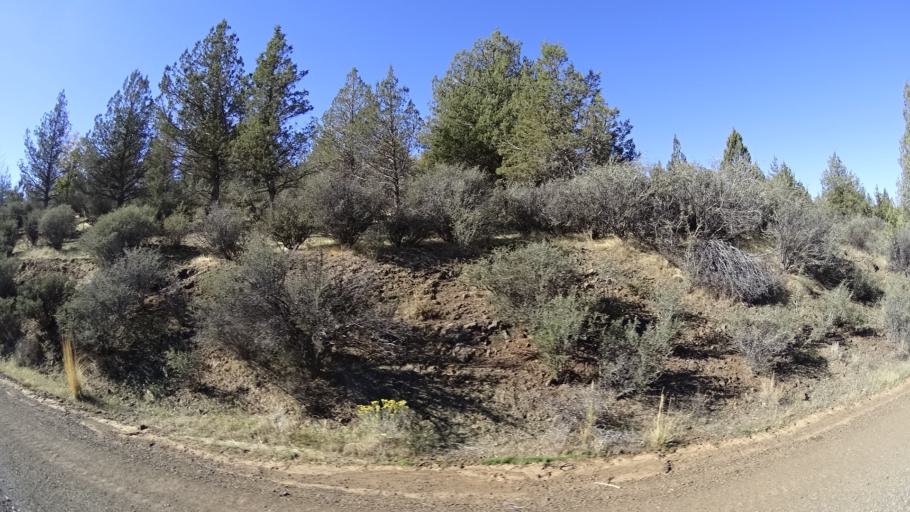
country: US
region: California
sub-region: Siskiyou County
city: Montague
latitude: 41.9141
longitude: -122.3733
